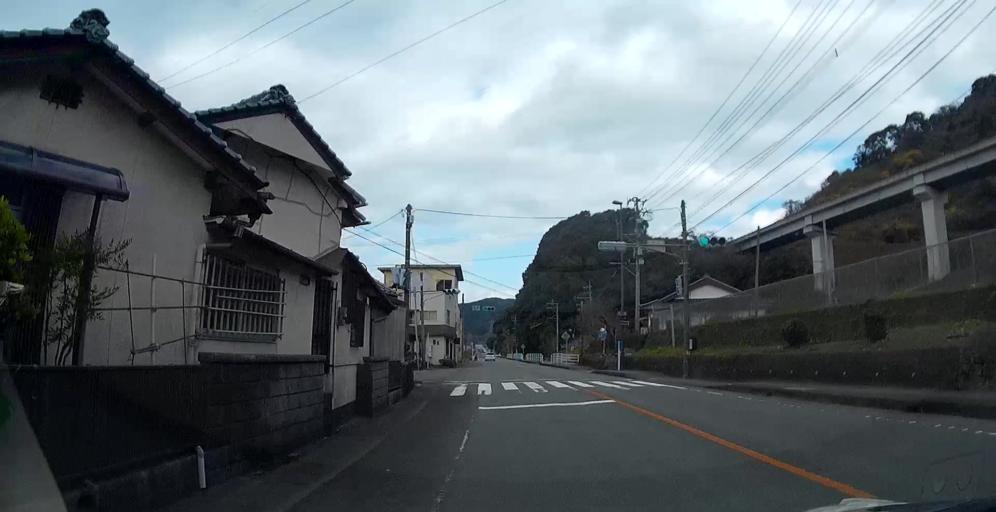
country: JP
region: Kumamoto
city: Minamata
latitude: 32.3539
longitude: 130.5078
